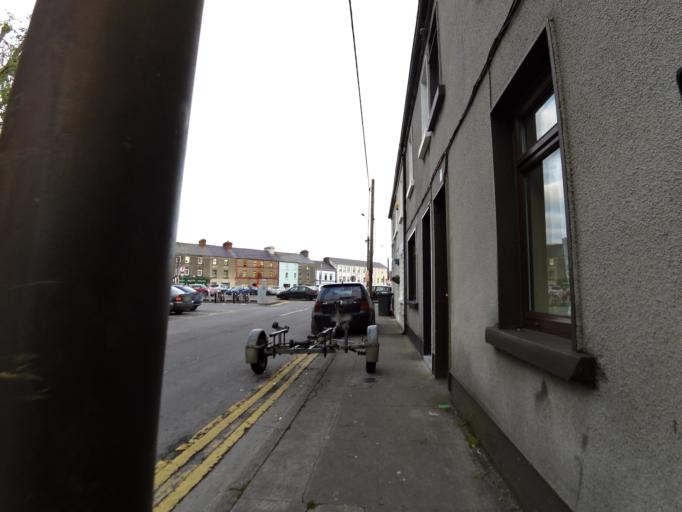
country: IE
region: Connaught
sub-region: County Galway
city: Gaillimh
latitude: 53.2765
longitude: -9.0533
